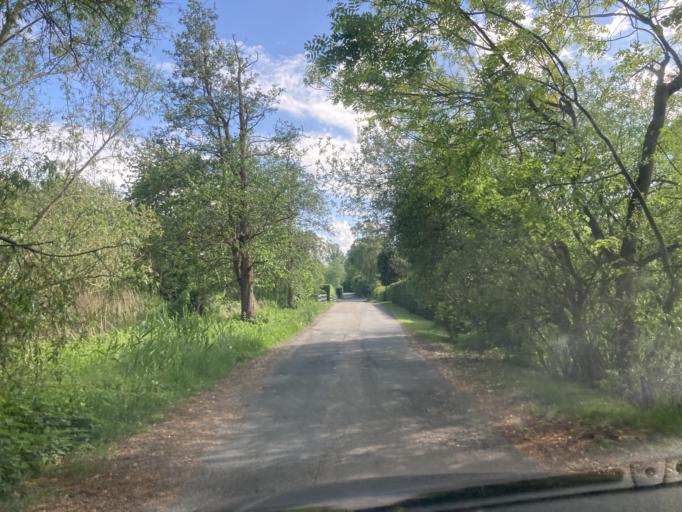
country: DK
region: Capital Region
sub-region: Gribskov Kommune
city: Helsinge
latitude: 56.0047
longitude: 12.1102
